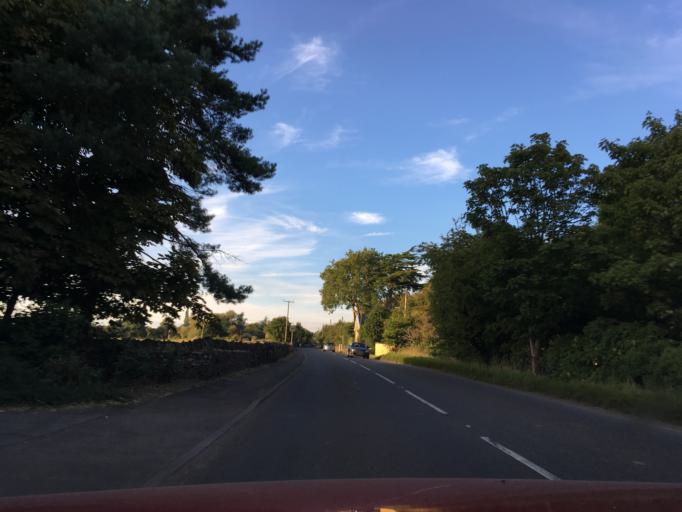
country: GB
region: England
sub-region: South Gloucestershire
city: Yate
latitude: 51.5624
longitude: -2.4503
